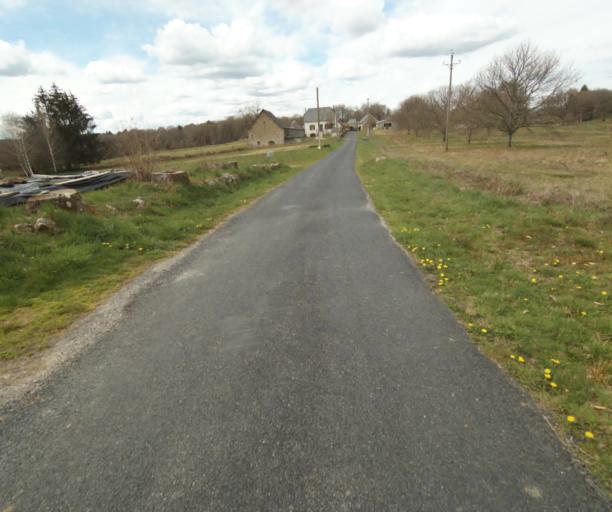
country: FR
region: Limousin
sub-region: Departement de la Correze
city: Argentat
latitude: 45.2183
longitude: 1.9228
